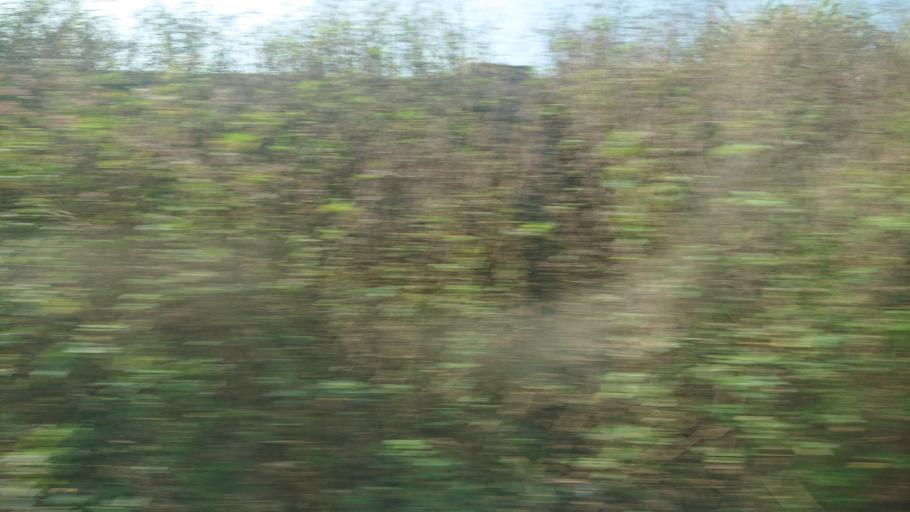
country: TW
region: Taiwan
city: Lugu
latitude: 23.7324
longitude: 120.6605
